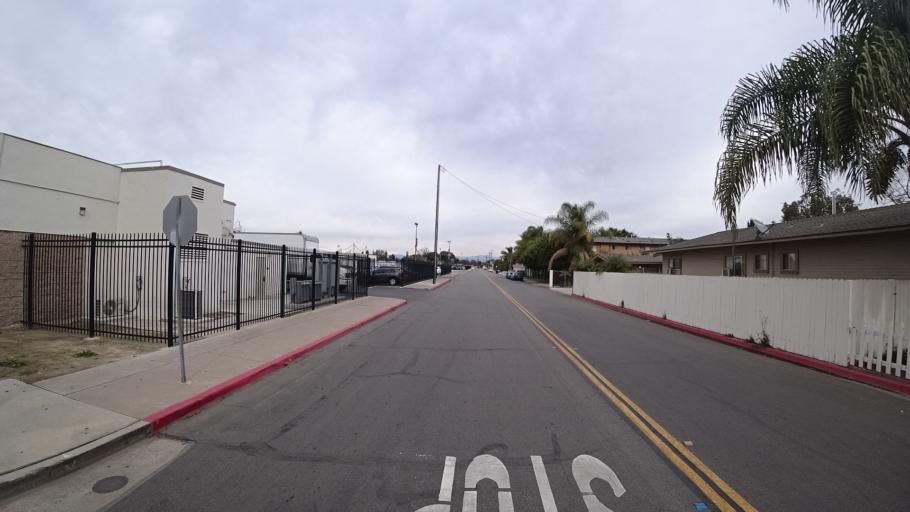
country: US
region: California
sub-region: Orange County
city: Garden Grove
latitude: 33.7780
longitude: -117.9345
